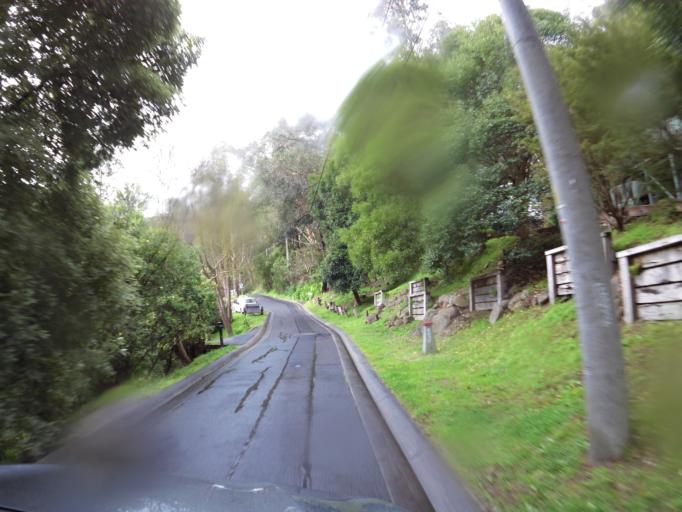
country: AU
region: Victoria
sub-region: Knox
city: The Basin
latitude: -37.8657
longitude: 145.3256
